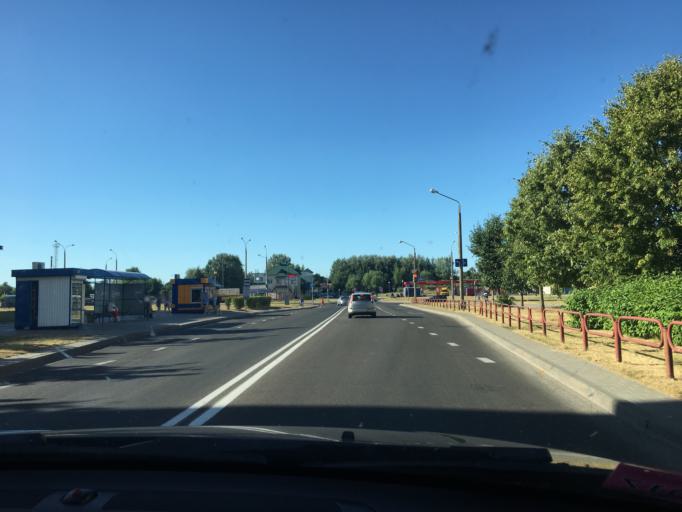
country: BY
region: Grodnenskaya
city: Hrodna
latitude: 53.7151
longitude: 23.8497
